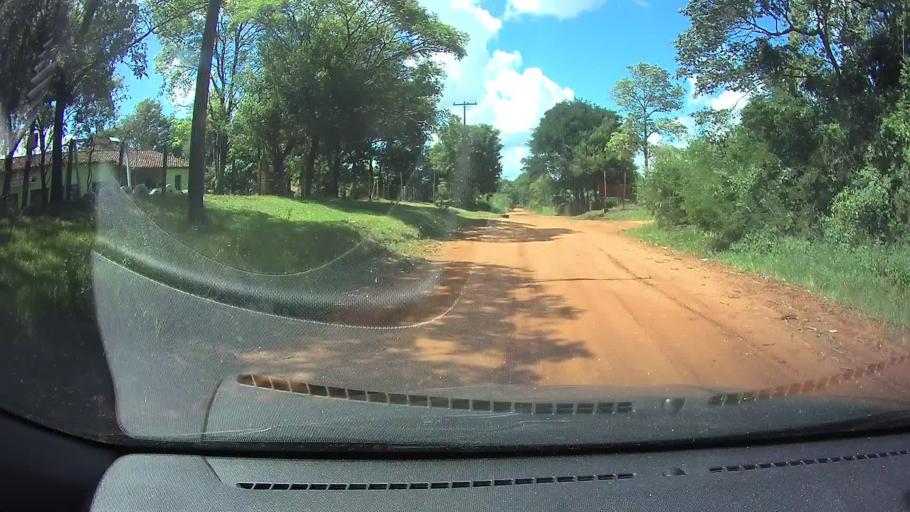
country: PY
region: Paraguari
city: La Colmena
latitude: -25.9441
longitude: -56.7797
